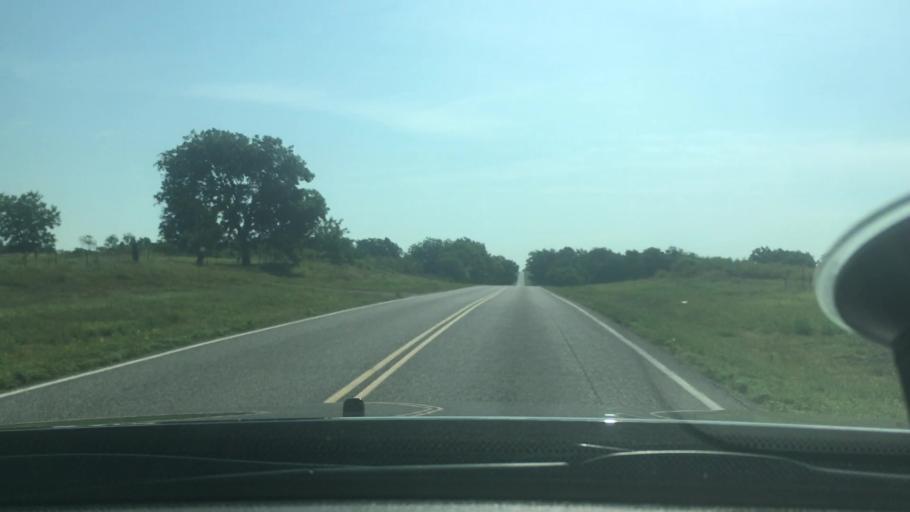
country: US
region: Oklahoma
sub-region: Garvin County
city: Pauls Valley
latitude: 34.6520
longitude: -97.2990
